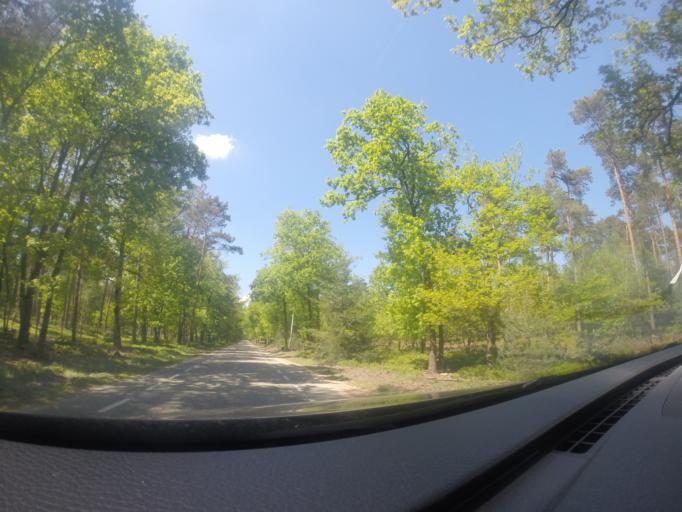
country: NL
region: Gelderland
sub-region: Gemeente Apeldoorn
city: Beekbergen
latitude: 52.1096
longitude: 5.9339
